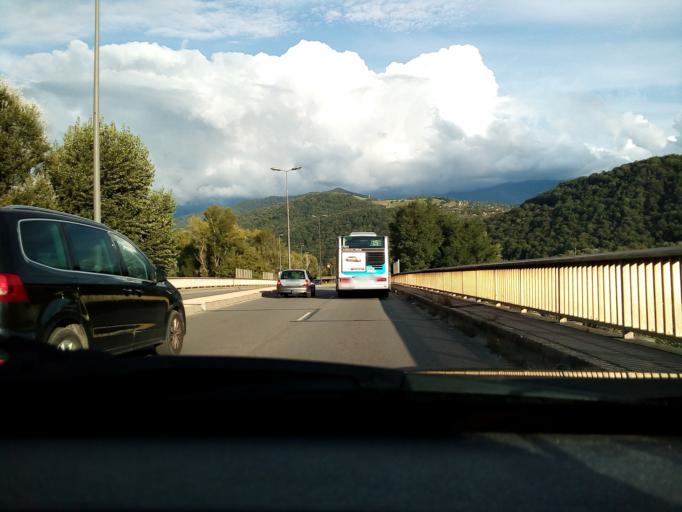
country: FR
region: Rhone-Alpes
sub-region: Departement de l'Isere
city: Gieres
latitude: 45.1828
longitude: 5.7751
